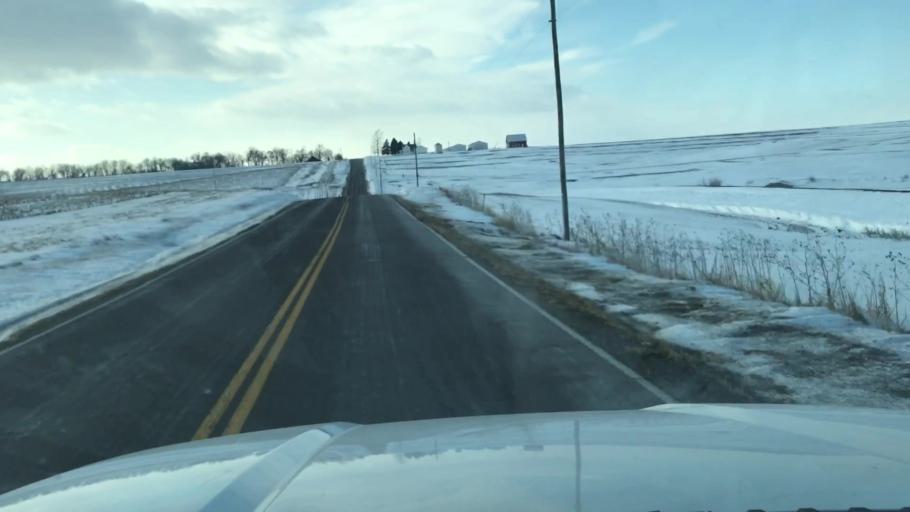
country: US
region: Missouri
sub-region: Nodaway County
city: Maryville
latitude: 40.2014
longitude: -94.9121
